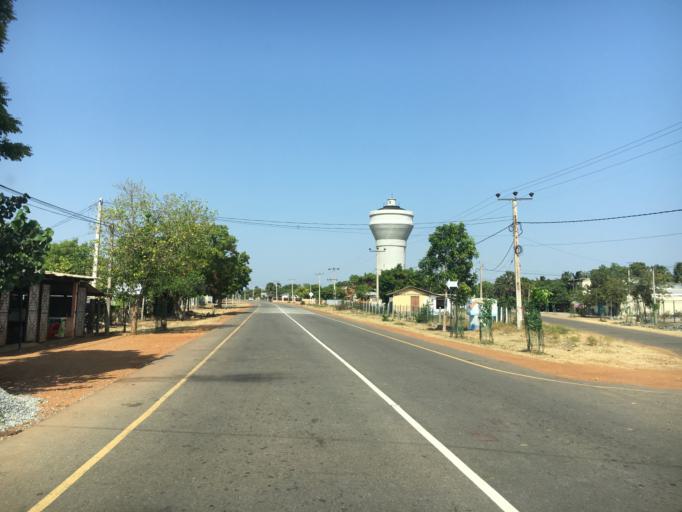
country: LK
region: Northern Province
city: Kilinochchi
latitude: 9.4379
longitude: 80.4062
